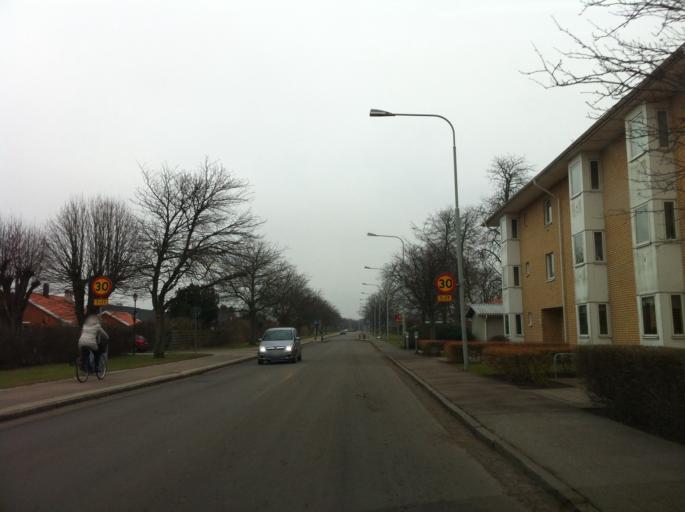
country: SE
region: Skane
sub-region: Landskrona
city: Landskrona
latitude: 55.8913
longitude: 12.8098
